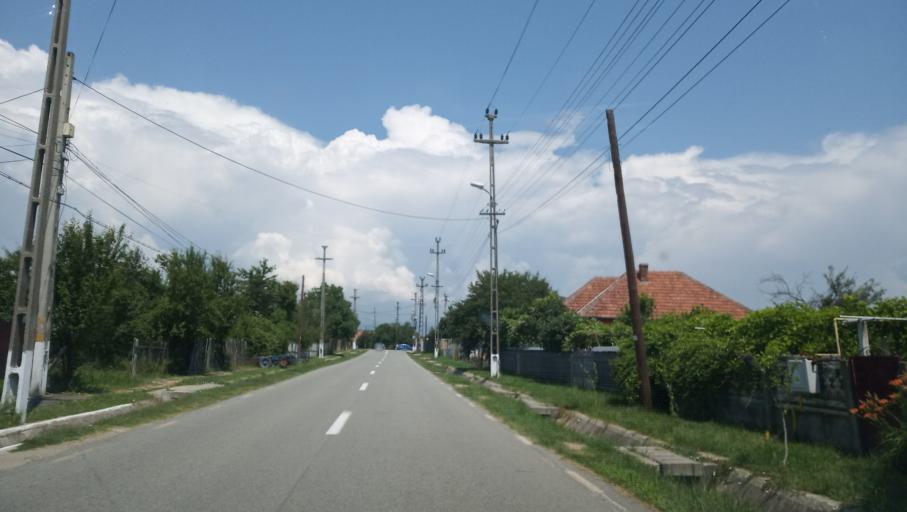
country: RO
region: Gorj
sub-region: Comuna Turcinesti
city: Turcinesti
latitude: 45.0665
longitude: 23.3471
